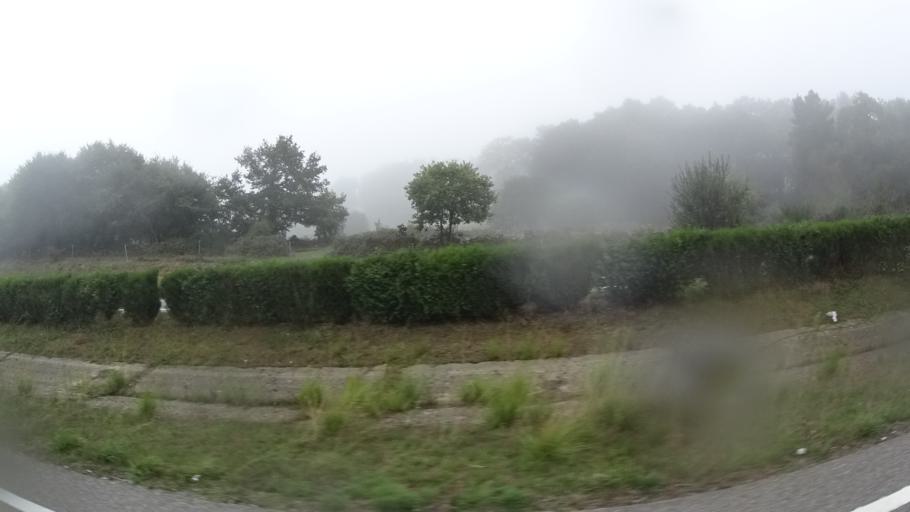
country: ES
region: Galicia
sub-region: Provincia de Lugo
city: Guitiriz
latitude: 43.1929
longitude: -7.8787
